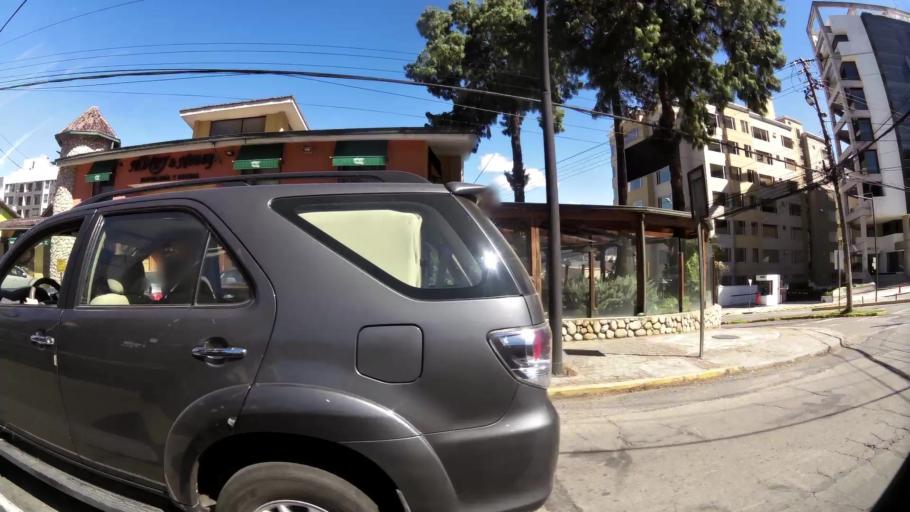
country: EC
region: Pichincha
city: Quito
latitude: -0.1819
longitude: -78.4757
